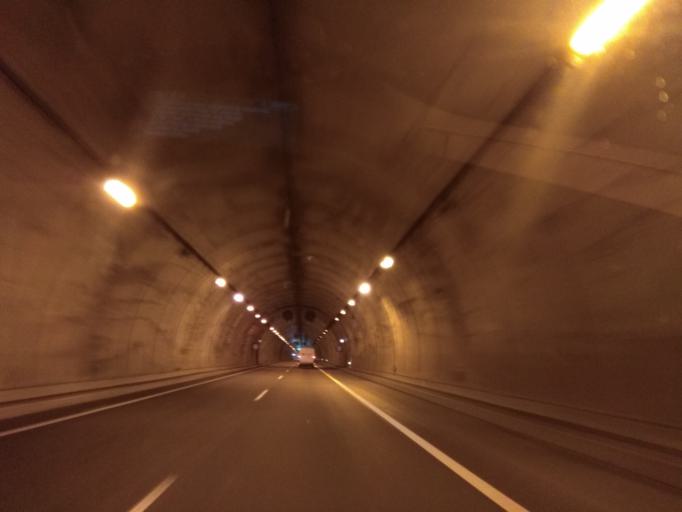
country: ES
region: Cantabria
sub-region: Provincia de Cantabria
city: Arenas de Iguna
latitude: 43.2114
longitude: -4.0767
